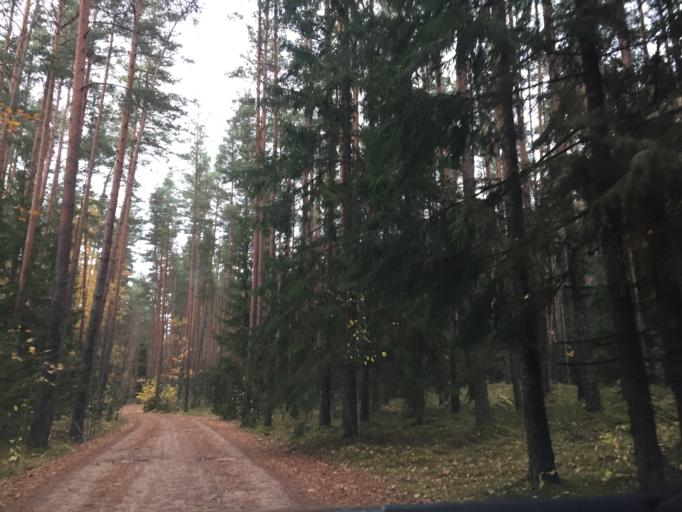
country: LV
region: Cesu Rajons
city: Cesis
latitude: 57.3592
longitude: 25.1757
